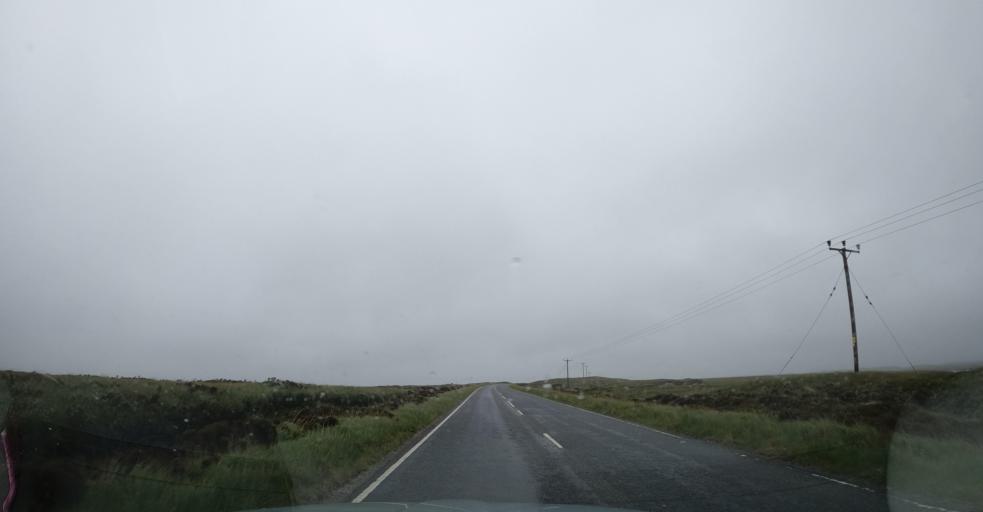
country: GB
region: Scotland
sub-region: Eilean Siar
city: Isle of North Uist
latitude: 57.5903
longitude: -7.2244
